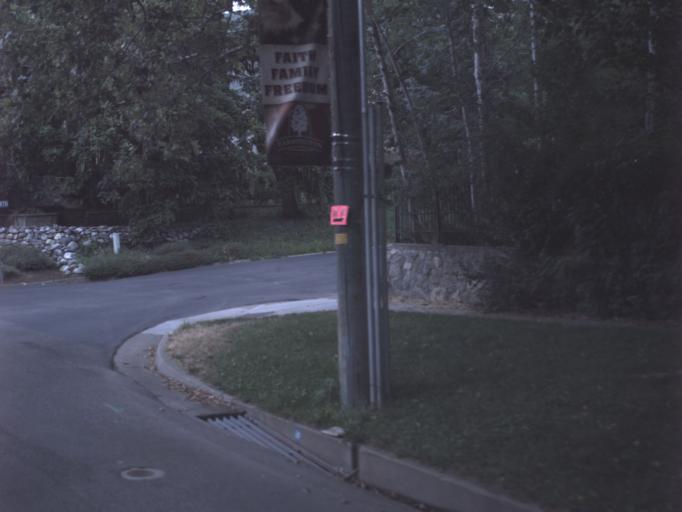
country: US
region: Utah
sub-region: Davis County
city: Farmington
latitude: 40.9885
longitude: -111.8875
